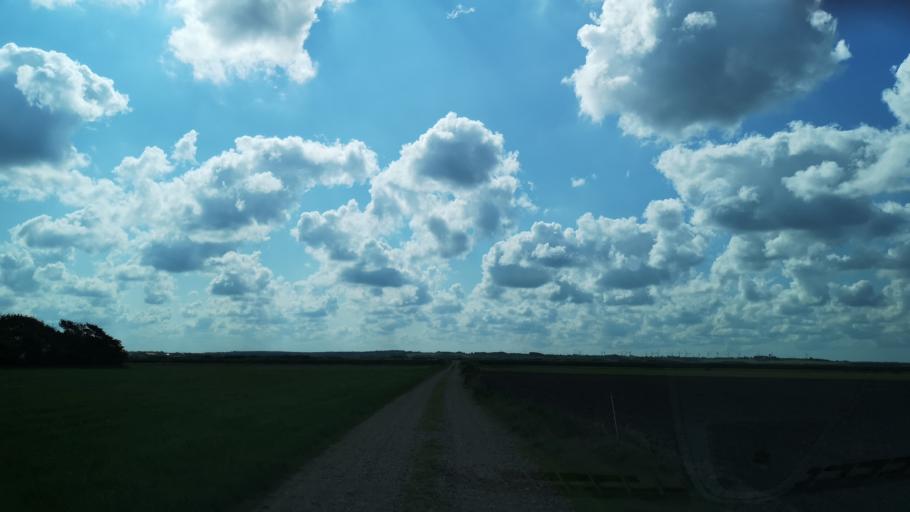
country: DK
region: Central Jutland
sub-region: Ringkobing-Skjern Kommune
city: Skjern
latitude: 55.9315
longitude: 8.4609
